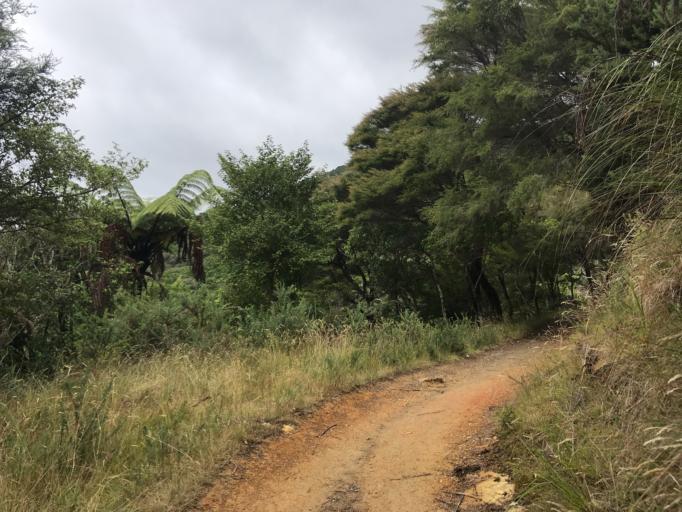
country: NZ
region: Marlborough
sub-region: Marlborough District
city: Picton
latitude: -41.2309
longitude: 173.9584
